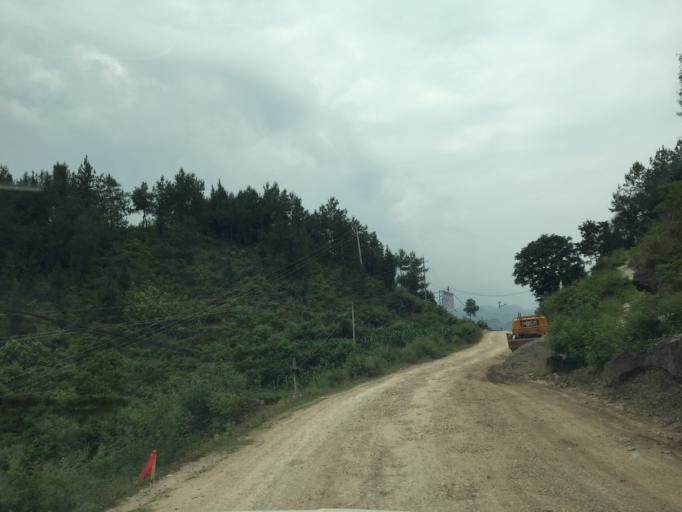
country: CN
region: Guizhou Sheng
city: Tongjing
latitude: 28.3684
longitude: 108.2345
